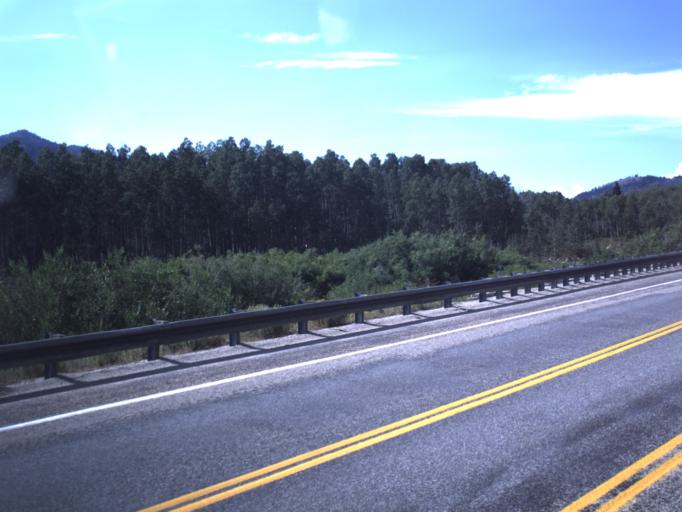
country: US
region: Utah
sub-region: Cache County
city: Richmond
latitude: 41.9292
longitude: -111.5614
